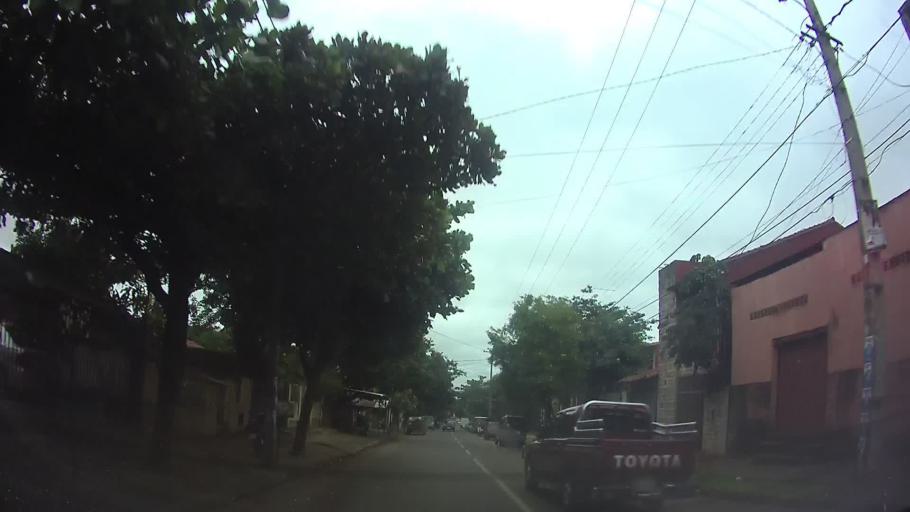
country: PY
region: Central
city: Lambare
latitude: -25.3331
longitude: -57.5814
